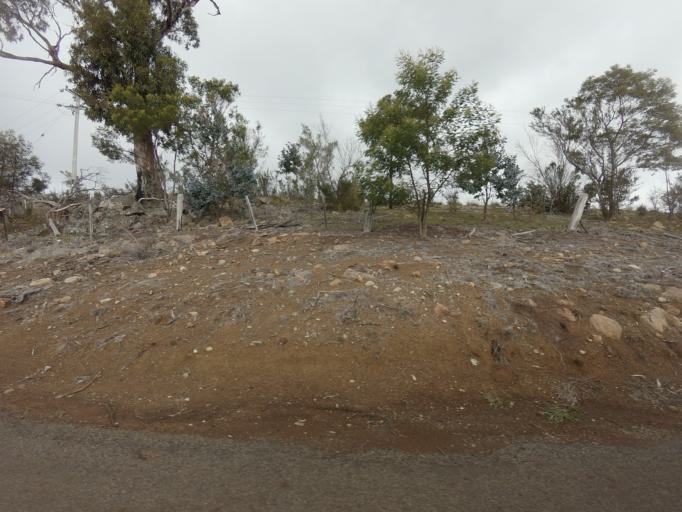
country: AU
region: Tasmania
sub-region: Sorell
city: Sorell
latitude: -42.5426
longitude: 147.9125
